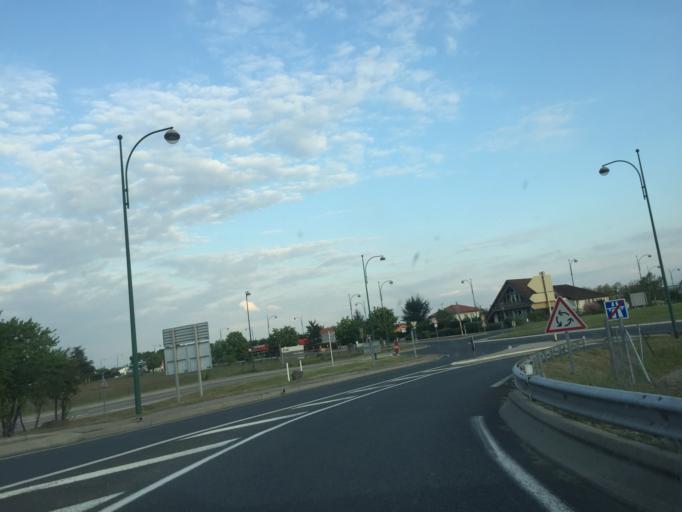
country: FR
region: Rhone-Alpes
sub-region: Departement de l'Ain
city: Balan
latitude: 45.8505
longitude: 5.1009
